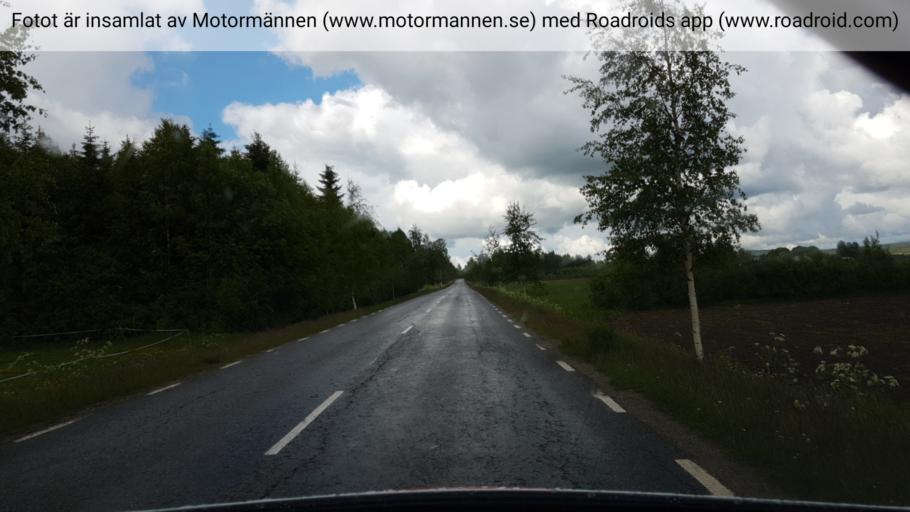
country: SE
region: Vaesterbotten
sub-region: Vannas Kommun
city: Vannasby
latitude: 63.8595
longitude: 19.9024
